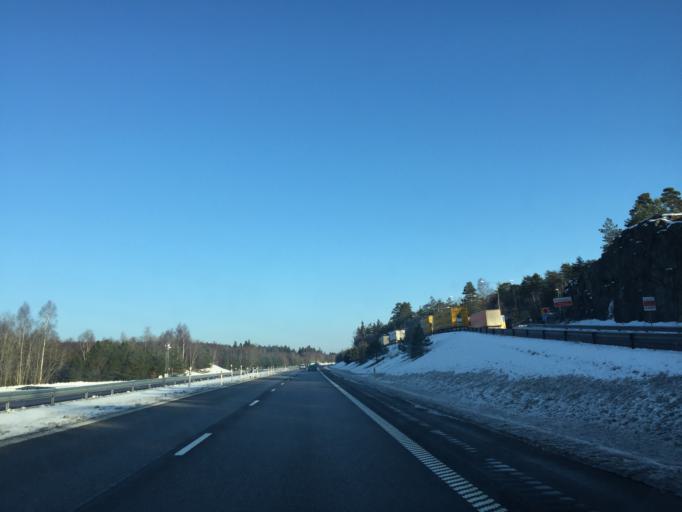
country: SE
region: Vaestra Goetaland
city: Svanesund
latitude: 58.1133
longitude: 11.8795
